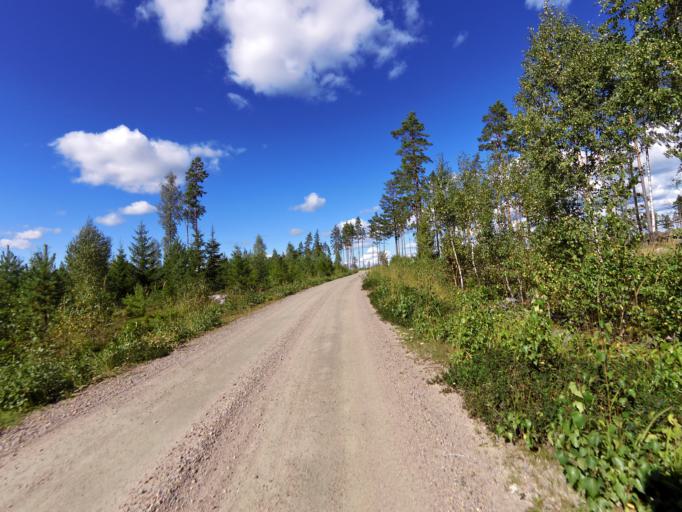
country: SE
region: Gaevleborg
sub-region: Ockelbo Kommun
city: Ockelbo
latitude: 60.7992
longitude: 16.8674
